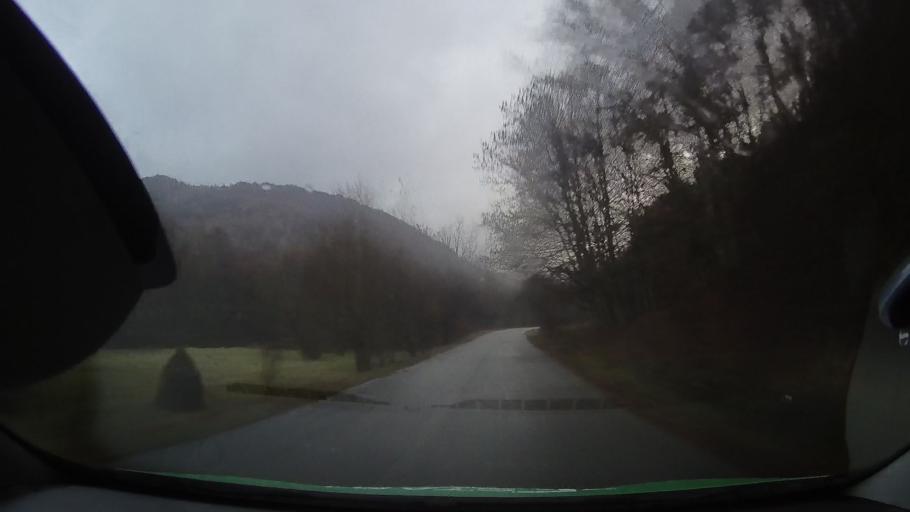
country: RO
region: Hunedoara
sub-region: Comuna Ribita
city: Ribita
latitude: 46.2698
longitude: 22.7432
